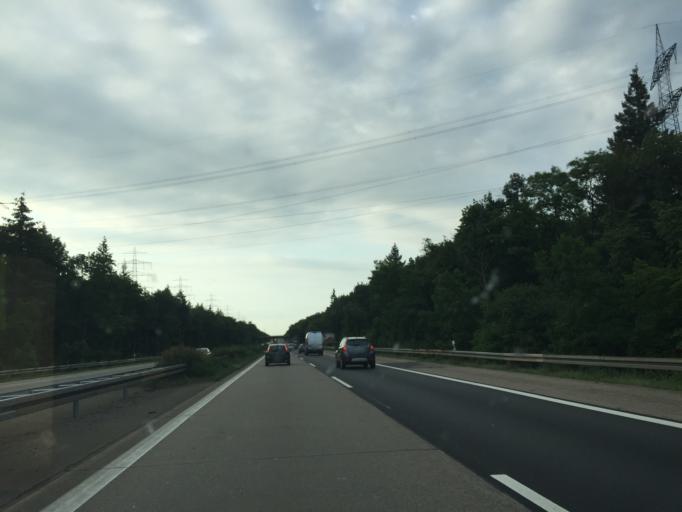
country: DE
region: Baden-Wuerttemberg
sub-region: Karlsruhe Region
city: Walldorf
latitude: 49.3313
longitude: 8.6302
